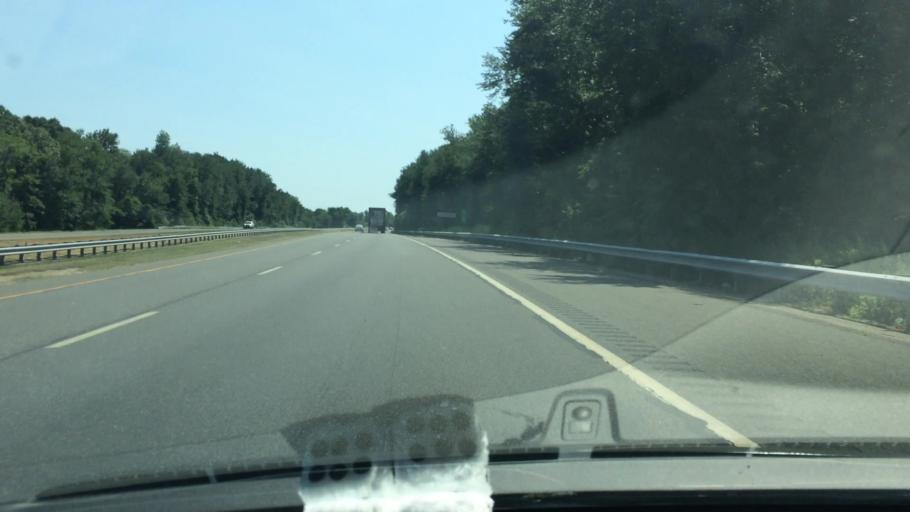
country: US
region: New Jersey
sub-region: Gloucester County
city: Gibbstown
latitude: 39.8016
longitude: -75.3144
